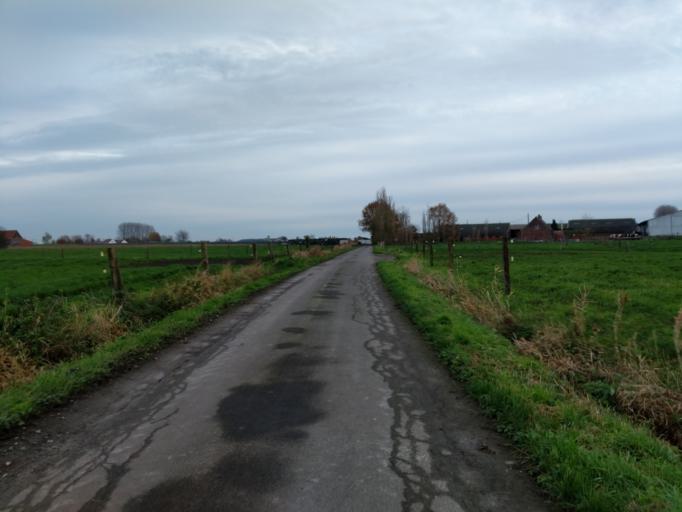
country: BE
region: Flanders
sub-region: Provincie West-Vlaanderen
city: Ruiselede
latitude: 51.0322
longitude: 3.4048
